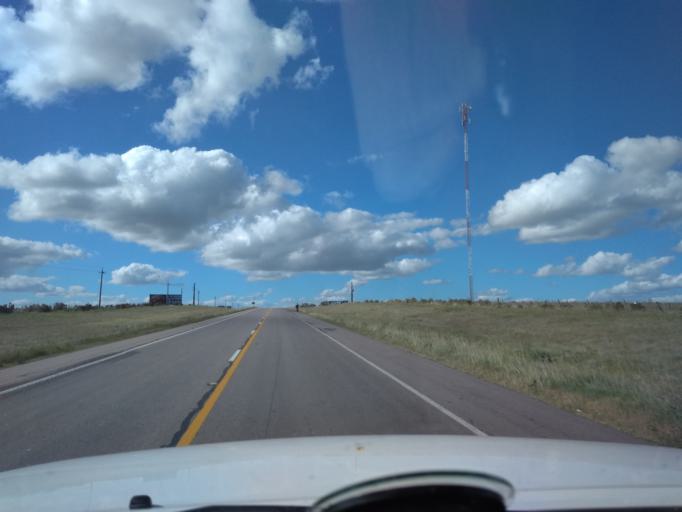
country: UY
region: Florida
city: Florida
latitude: -34.2017
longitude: -56.2014
